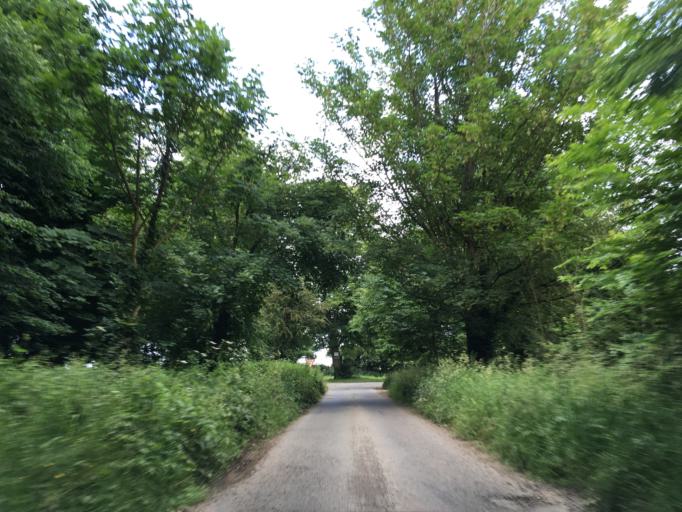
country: GB
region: England
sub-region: Gloucestershire
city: Tetbury
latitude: 51.6593
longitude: -2.1905
